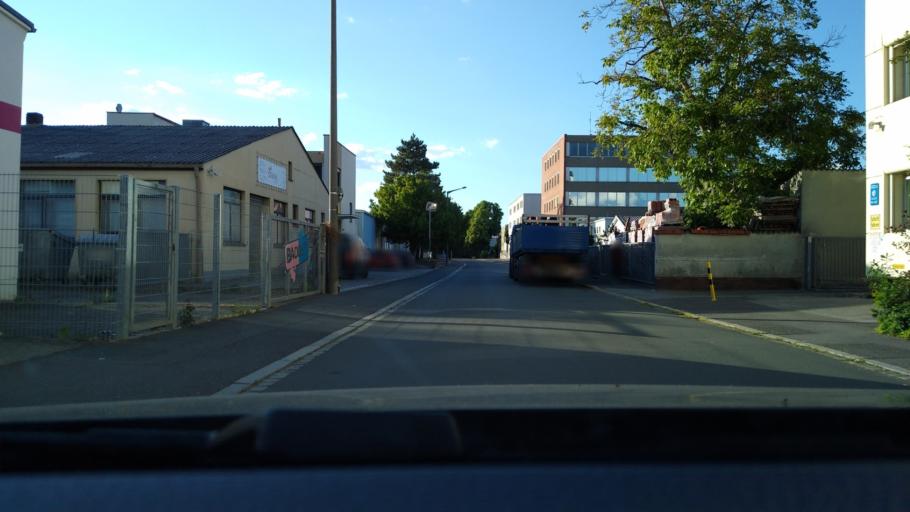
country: DE
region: Bavaria
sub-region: Regierungsbezirk Mittelfranken
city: Furth
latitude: 49.4798
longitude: 10.9674
